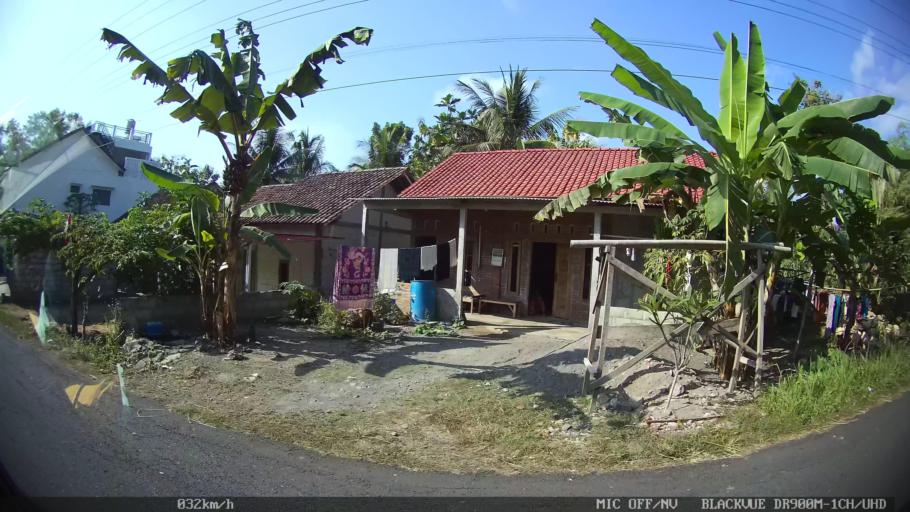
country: ID
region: Daerah Istimewa Yogyakarta
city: Kasihan
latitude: -7.8356
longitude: 110.2837
